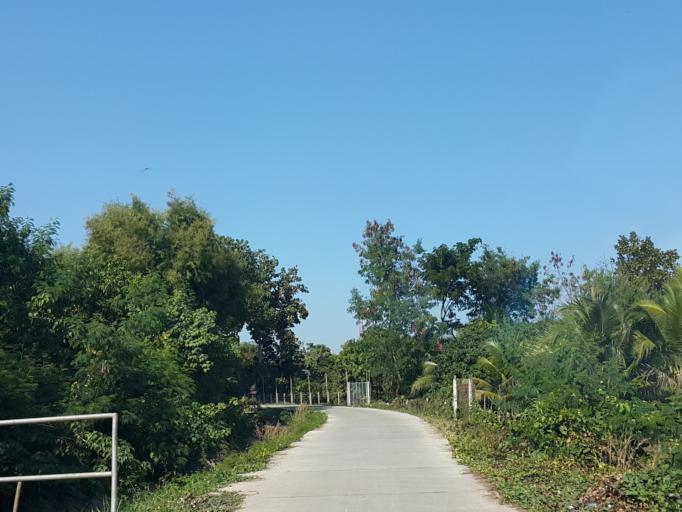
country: TH
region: Chiang Mai
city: San Sai
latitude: 18.8613
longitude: 98.9859
